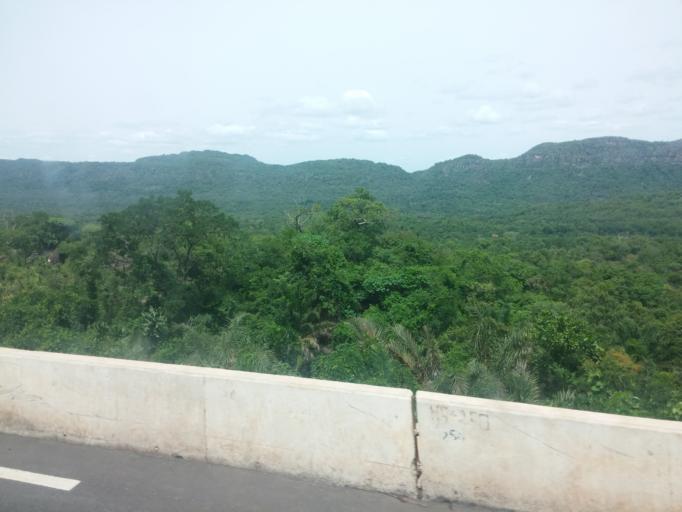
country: TG
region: Kara
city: Bafilo
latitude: 9.2572
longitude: 1.2253
